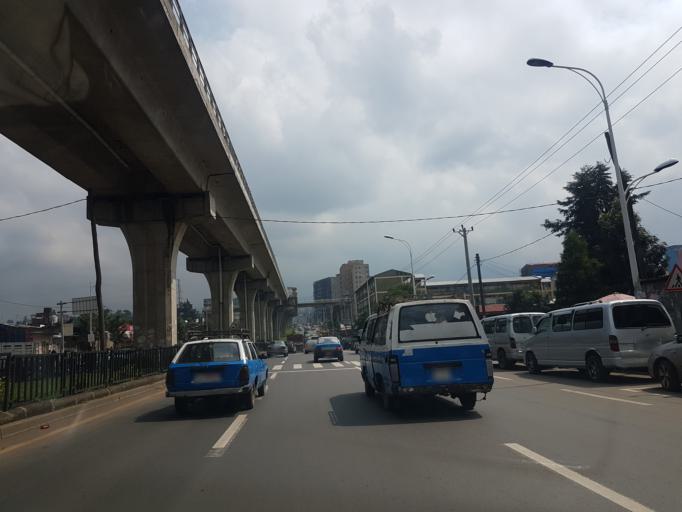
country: ET
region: Adis Abeba
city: Addis Ababa
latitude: 9.0138
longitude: 38.7346
